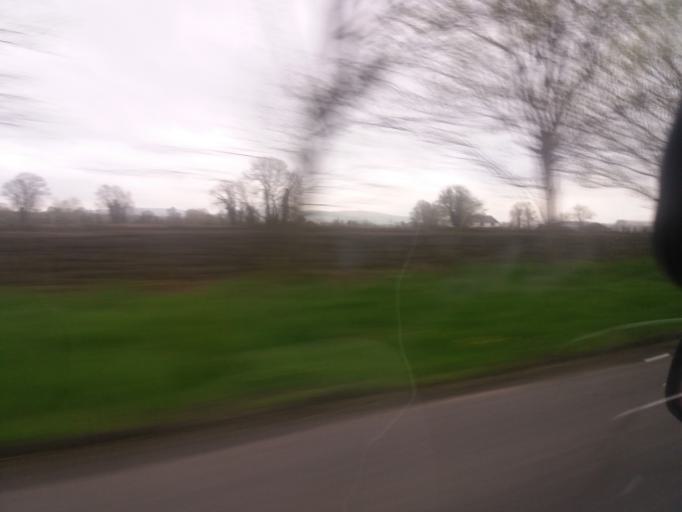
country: IE
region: Munster
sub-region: County Limerick
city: Adare
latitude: 52.5409
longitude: -8.8586
